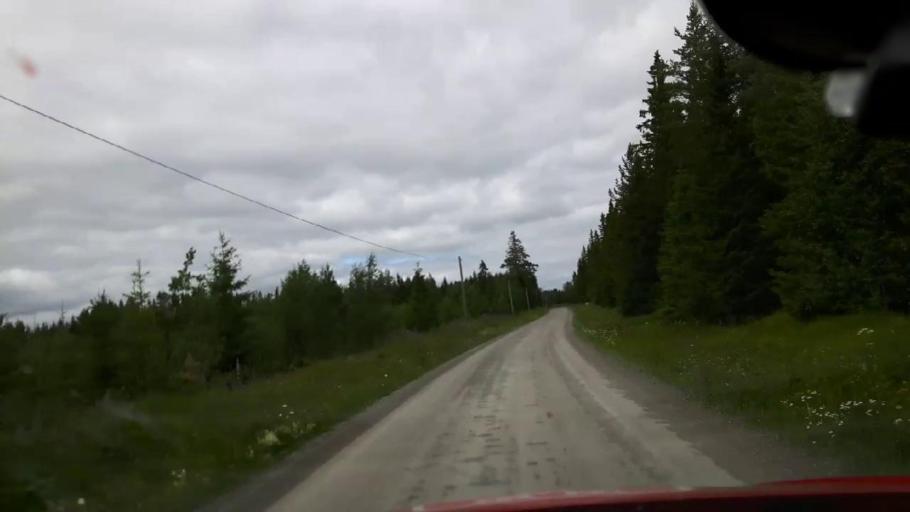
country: SE
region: Jaemtland
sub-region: OEstersunds Kommun
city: Brunflo
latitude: 63.0664
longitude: 14.8955
